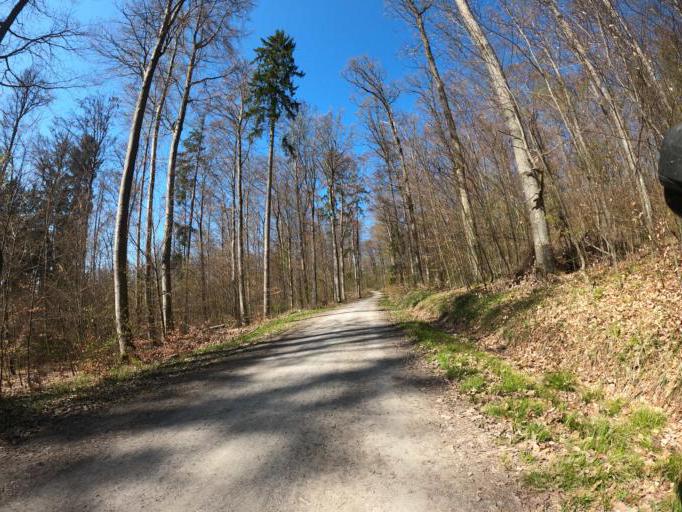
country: DE
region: Baden-Wuerttemberg
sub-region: Karlsruhe Region
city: Wiernsheim
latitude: 48.8938
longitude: 8.8277
